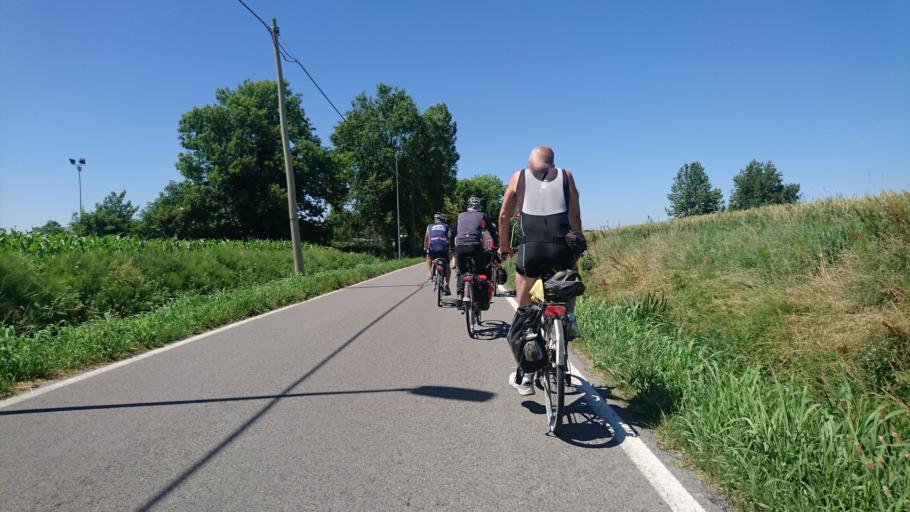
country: IT
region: Veneto
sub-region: Provincia di Padova
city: Bertipaglia
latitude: 45.3080
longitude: 11.8870
